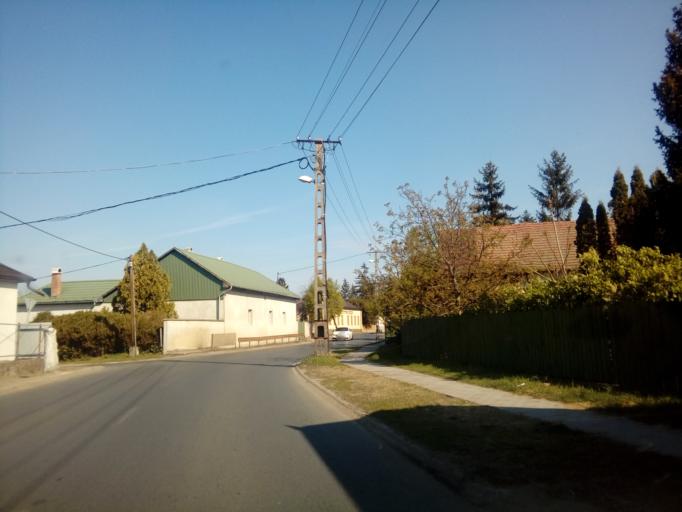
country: HU
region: Szabolcs-Szatmar-Bereg
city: Nagykallo
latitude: 47.8712
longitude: 21.8468
